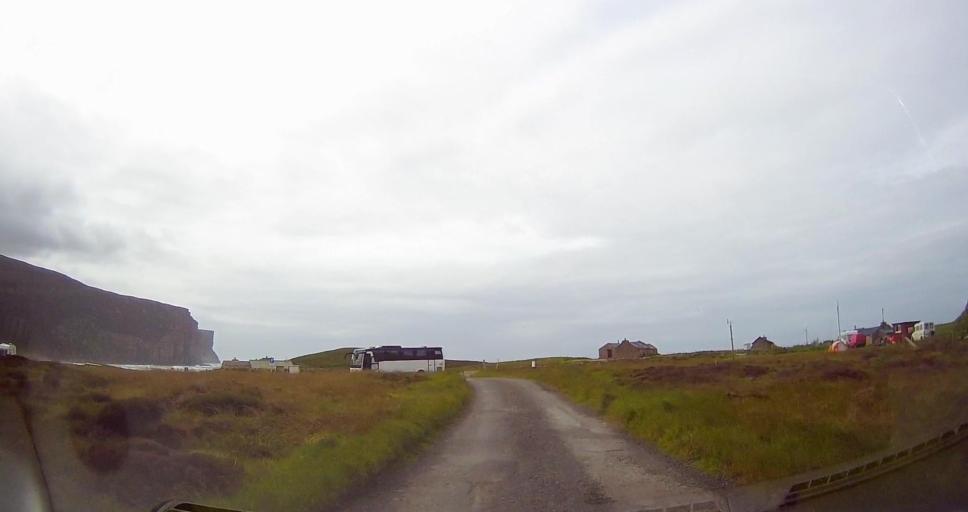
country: GB
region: Scotland
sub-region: Orkney Islands
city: Stromness
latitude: 58.8740
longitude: -3.3860
